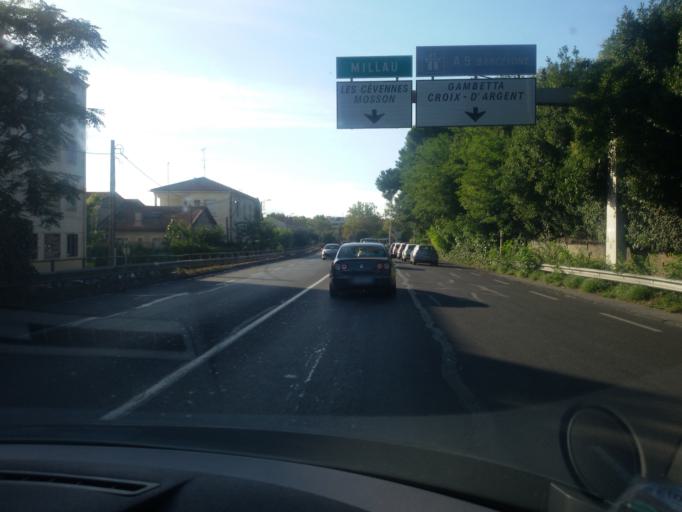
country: FR
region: Languedoc-Roussillon
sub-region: Departement de l'Herault
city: Montpellier
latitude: 43.5994
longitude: 3.8713
